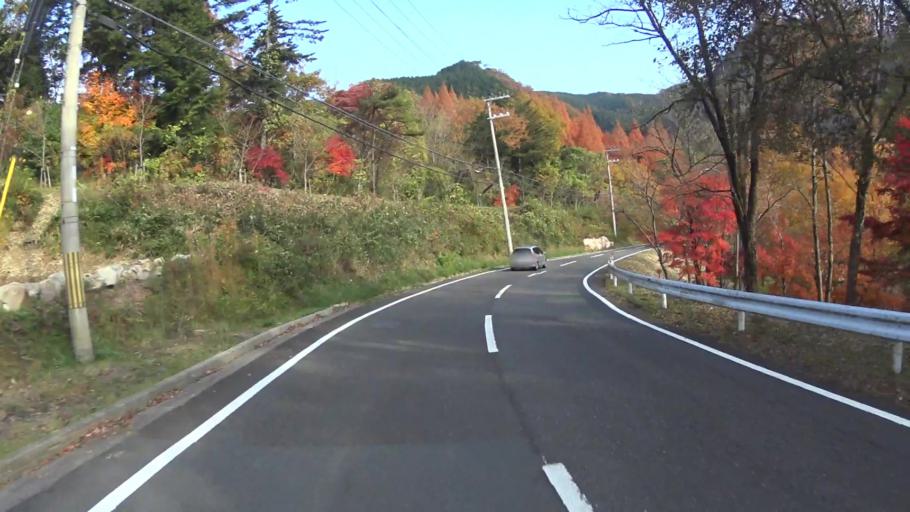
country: JP
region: Kyoto
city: Maizuru
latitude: 35.5330
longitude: 135.3929
